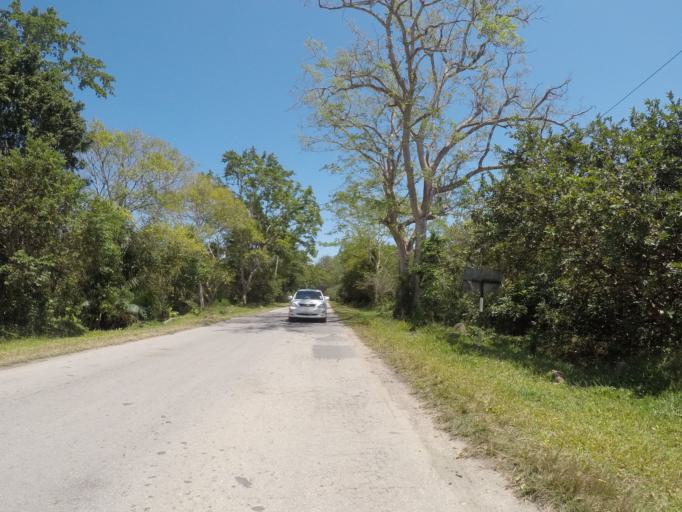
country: TZ
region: Zanzibar Central/South
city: Nganane
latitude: -6.2735
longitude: 39.4183
